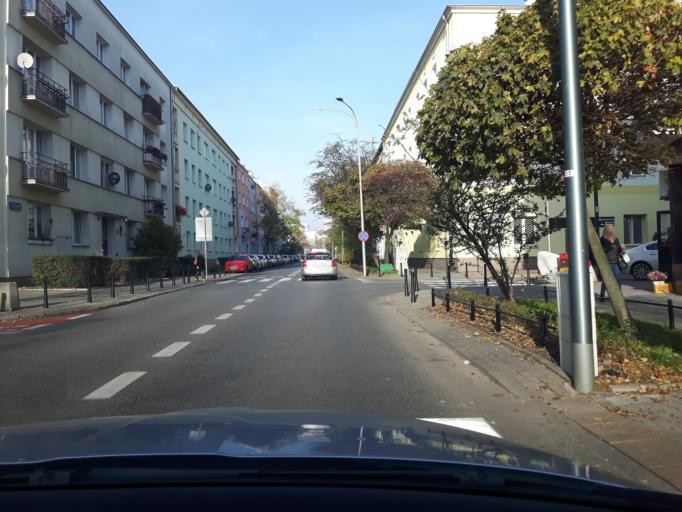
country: PL
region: Masovian Voivodeship
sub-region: Warszawa
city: Ochota
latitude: 52.2155
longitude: 20.9755
